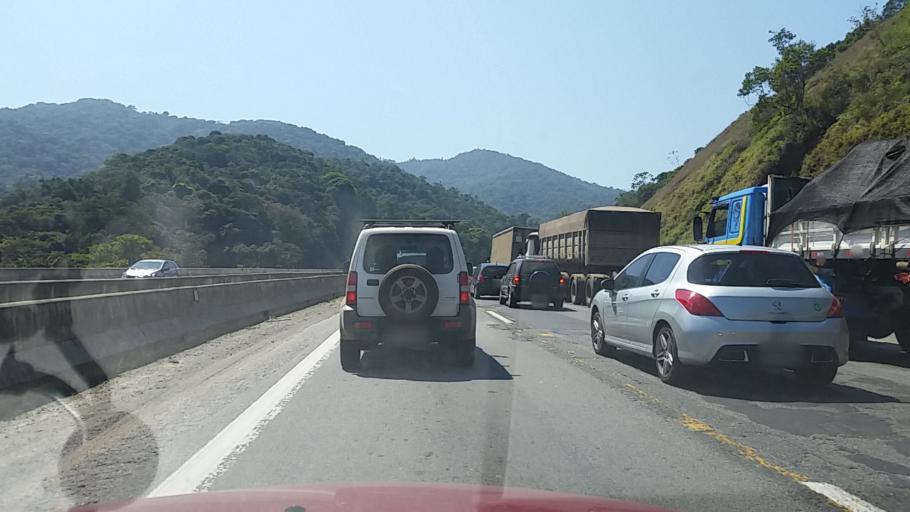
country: BR
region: Sao Paulo
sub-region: Juquitiba
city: Juquitiba
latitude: -24.0758
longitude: -47.2505
